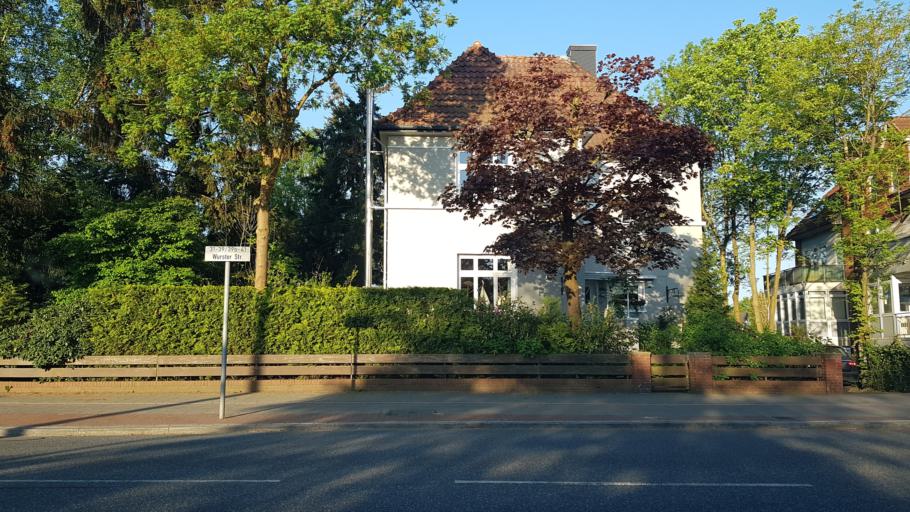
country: DE
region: Bremen
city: Bremerhaven
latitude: 53.5737
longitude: 8.5933
